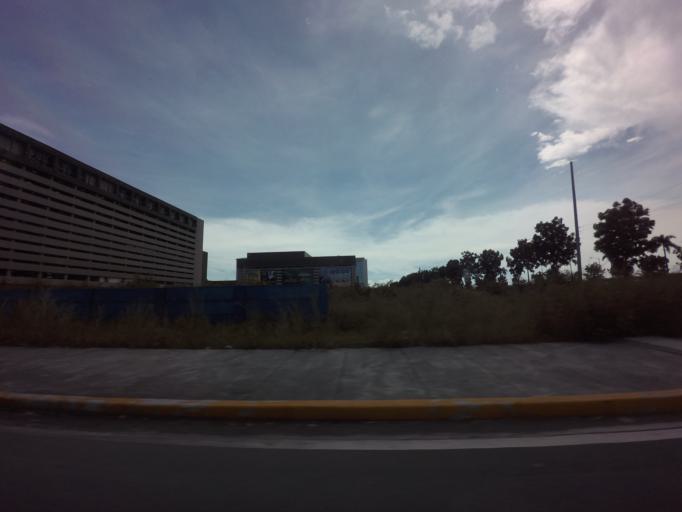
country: PH
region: Metro Manila
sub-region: Makati City
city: Makati City
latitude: 14.5242
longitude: 120.9853
